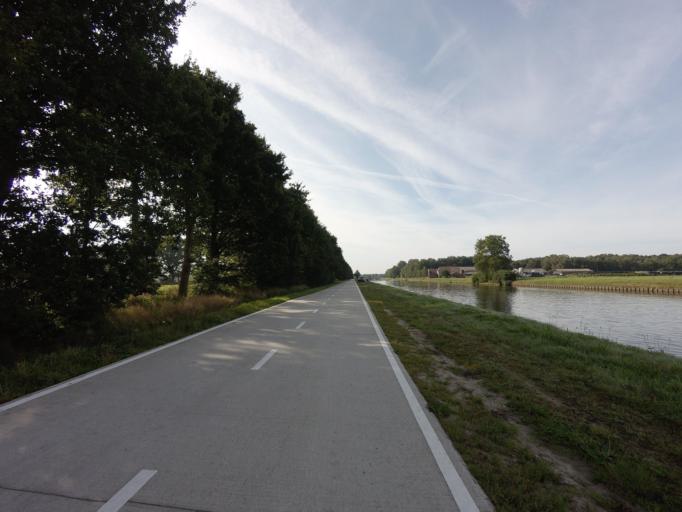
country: NL
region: Drenthe
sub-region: Gemeente Tynaarlo
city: Tynaarlo
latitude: 53.0423
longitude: 6.6080
